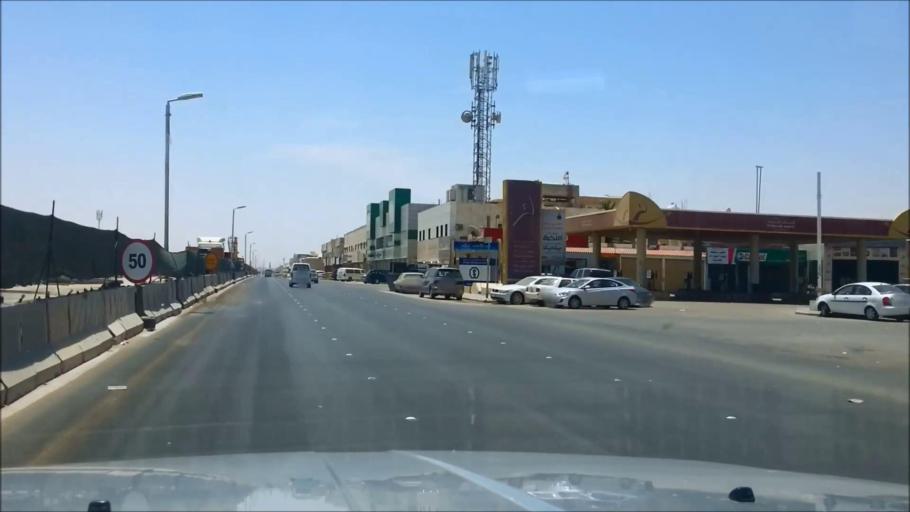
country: SA
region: Ar Riyad
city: Riyadh
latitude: 24.7584
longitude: 46.6740
